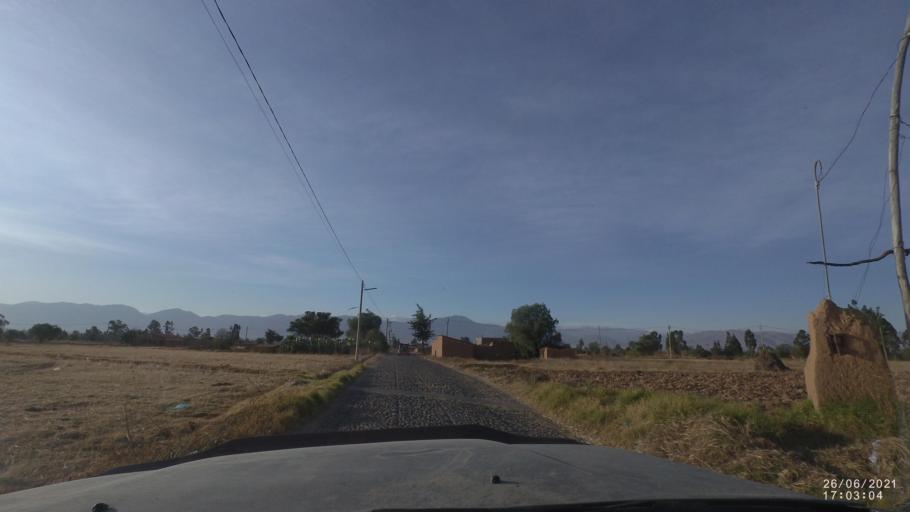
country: BO
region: Cochabamba
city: Cliza
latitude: -17.6470
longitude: -65.9123
